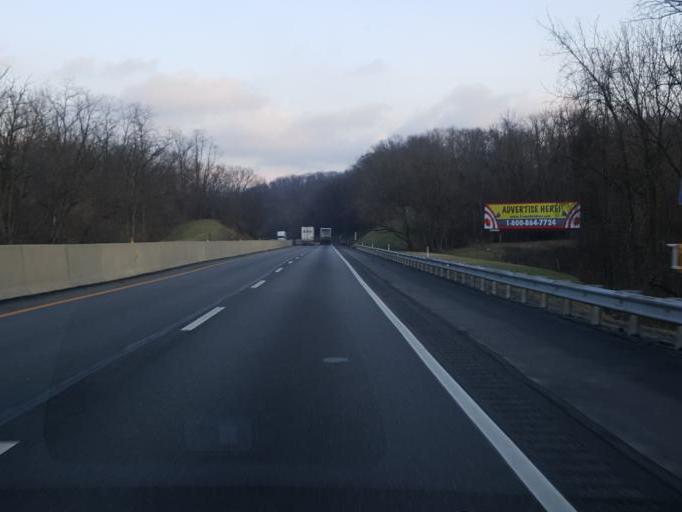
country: US
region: Pennsylvania
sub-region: Cumberland County
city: Shiremanstown
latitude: 40.1976
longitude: -76.9372
